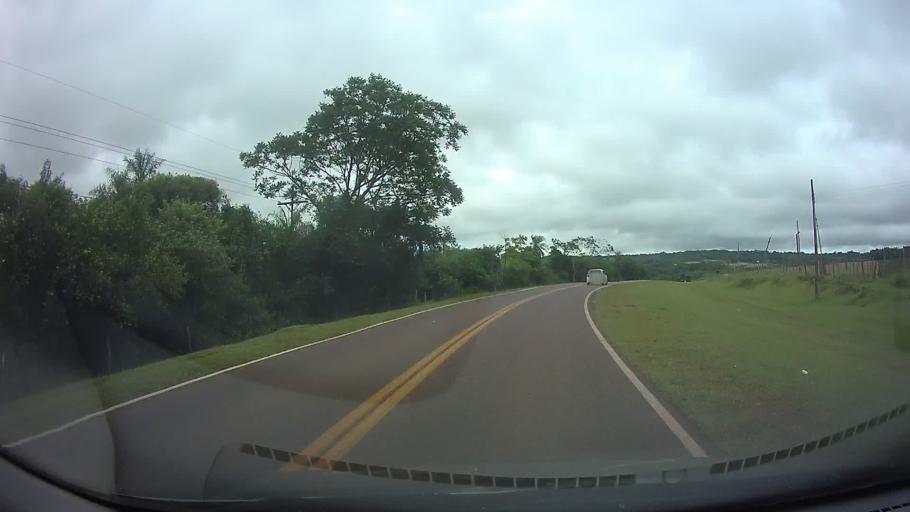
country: PY
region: Paraguari
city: Acahay
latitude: -25.9232
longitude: -57.1066
